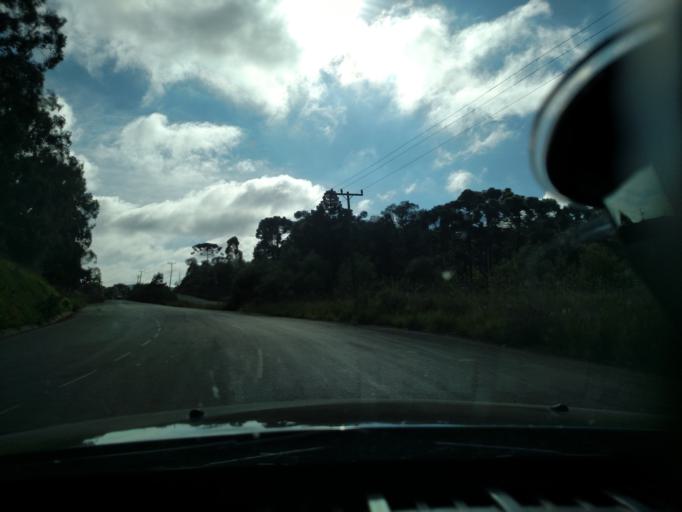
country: BR
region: Rio Grande do Sul
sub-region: Vacaria
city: Estrela
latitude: -27.9022
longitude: -50.7499
